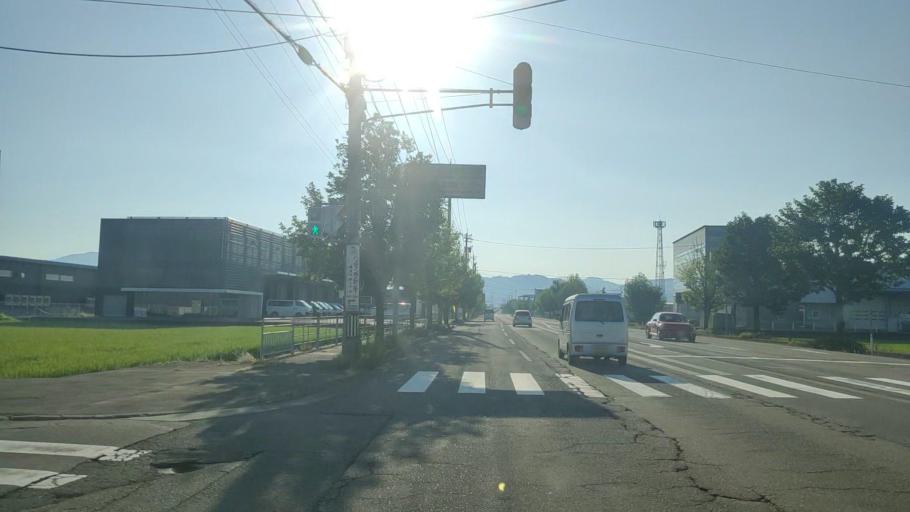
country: JP
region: Fukui
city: Fukui-shi
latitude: 36.0859
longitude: 136.2556
